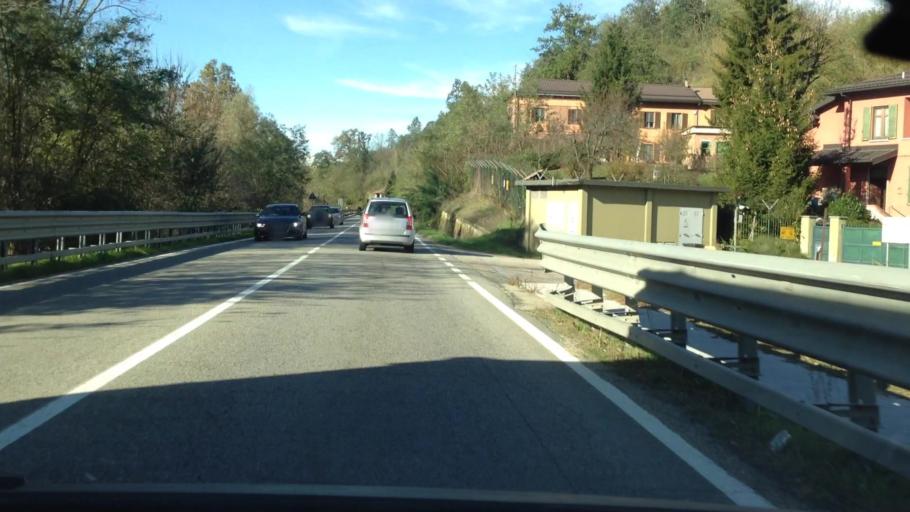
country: IT
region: Piedmont
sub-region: Provincia di Asti
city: Castello di Annone
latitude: 44.8852
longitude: 8.3105
